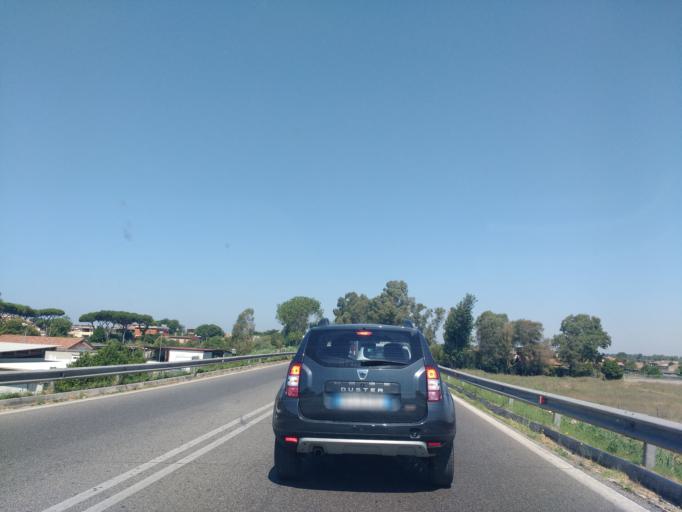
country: IT
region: Latium
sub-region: Citta metropolitana di Roma Capitale
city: Lido di Ostia
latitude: 41.7566
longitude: 12.2757
